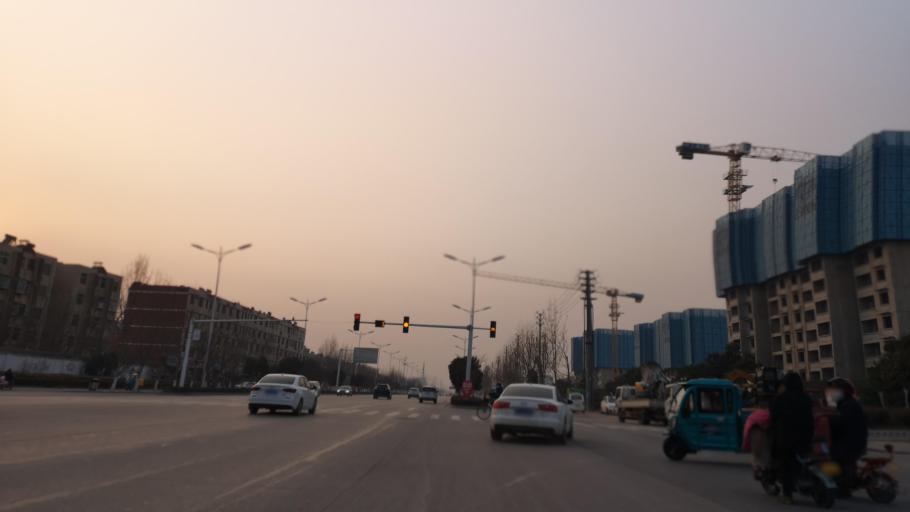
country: CN
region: Henan Sheng
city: Zhongyuanlu
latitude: 35.7895
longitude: 115.0828
